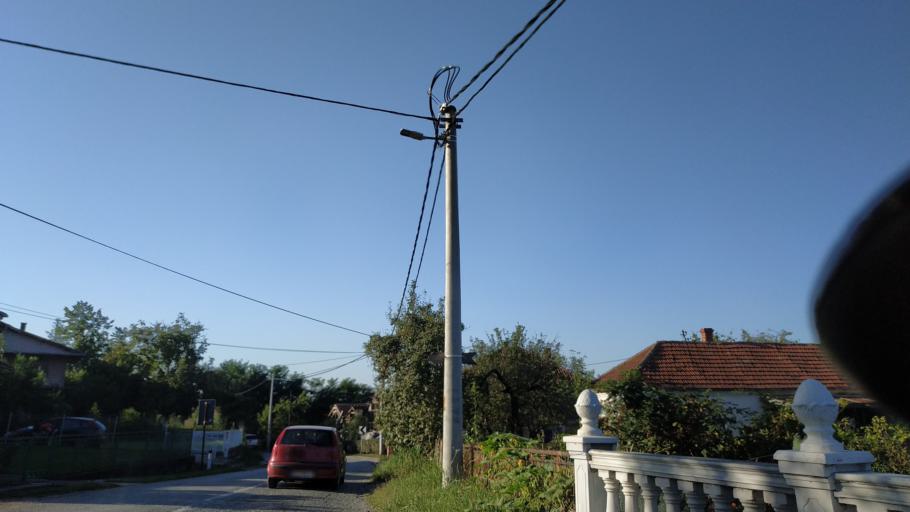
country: RS
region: Central Serbia
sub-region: Rasinski Okrug
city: Krusevac
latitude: 43.4920
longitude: 21.3448
